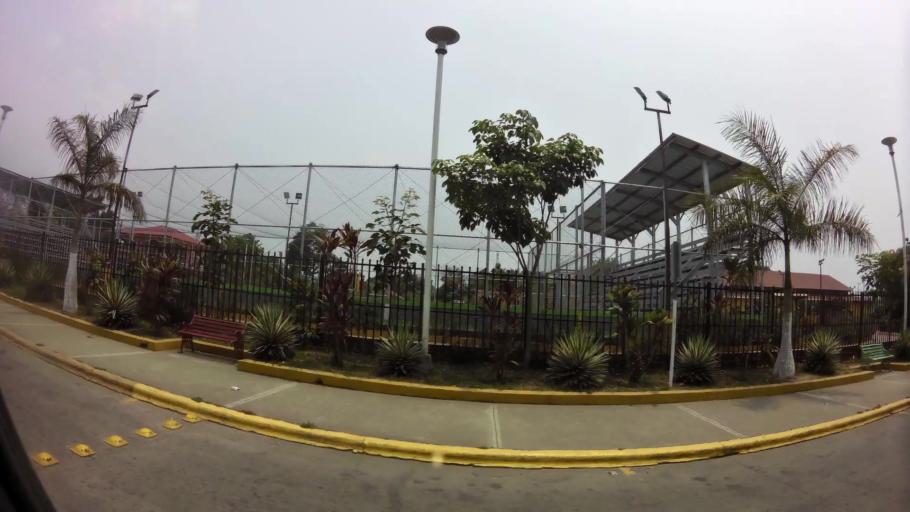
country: HN
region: Yoro
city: El Progreso
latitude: 15.3946
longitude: -87.8096
